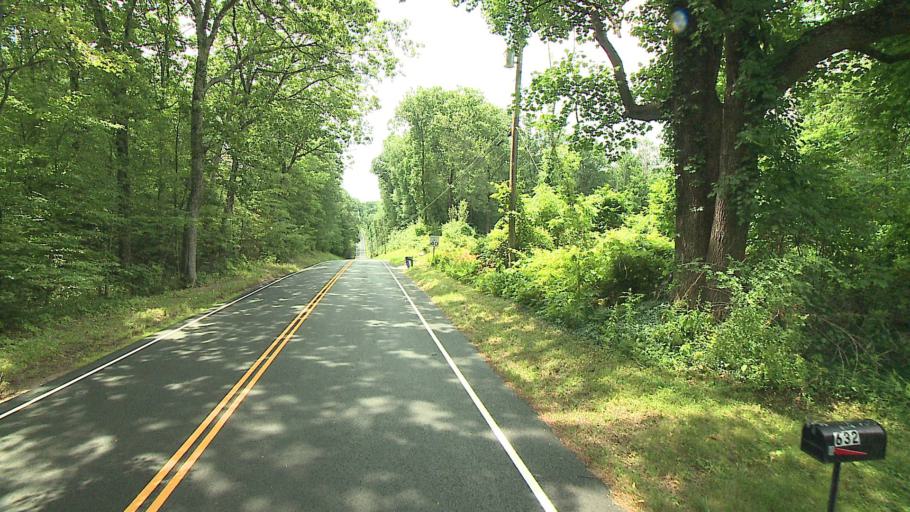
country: US
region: Massachusetts
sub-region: Hampden County
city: Granville
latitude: 42.0364
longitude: -72.8834
